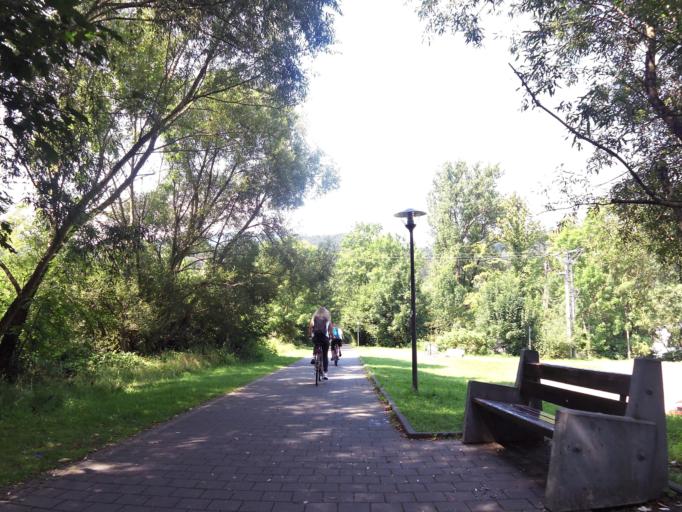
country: PL
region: Silesian Voivodeship
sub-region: Powiat zywiecki
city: Wegierska Gorka
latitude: 49.6026
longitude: 19.1086
